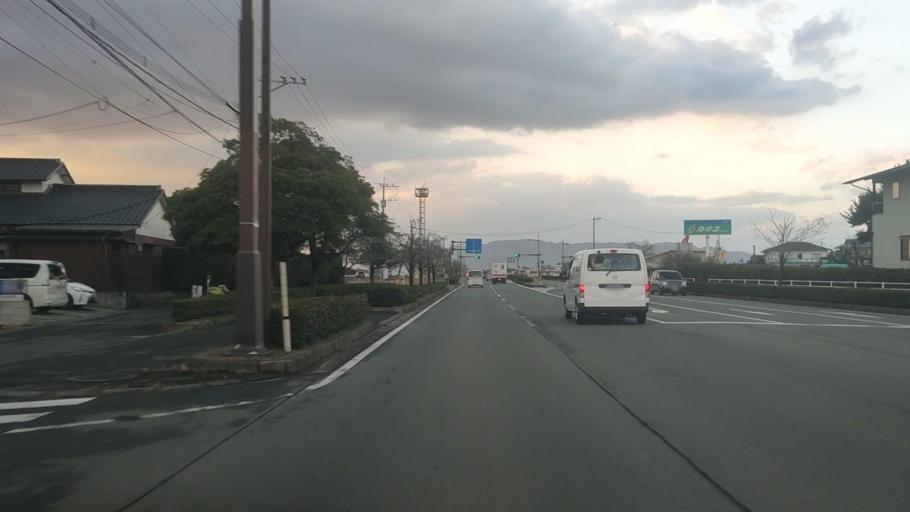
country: JP
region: Kumamoto
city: Kumamoto
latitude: 32.7592
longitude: 130.7059
